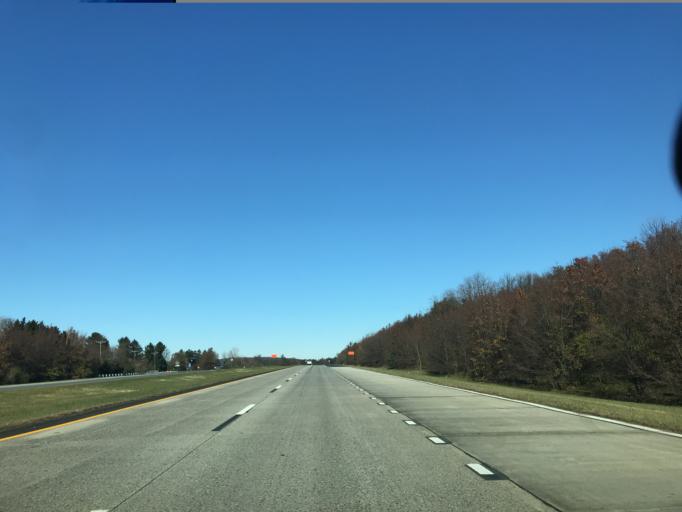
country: US
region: Delaware
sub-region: New Castle County
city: Glasgow
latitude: 39.5893
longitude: -75.7404
